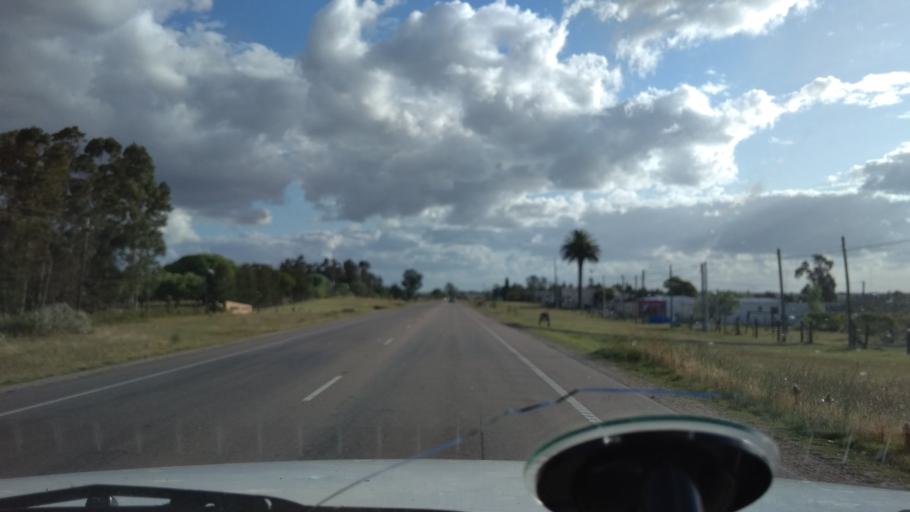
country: UY
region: Canelones
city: San Jacinto
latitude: -34.5290
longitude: -55.8505
